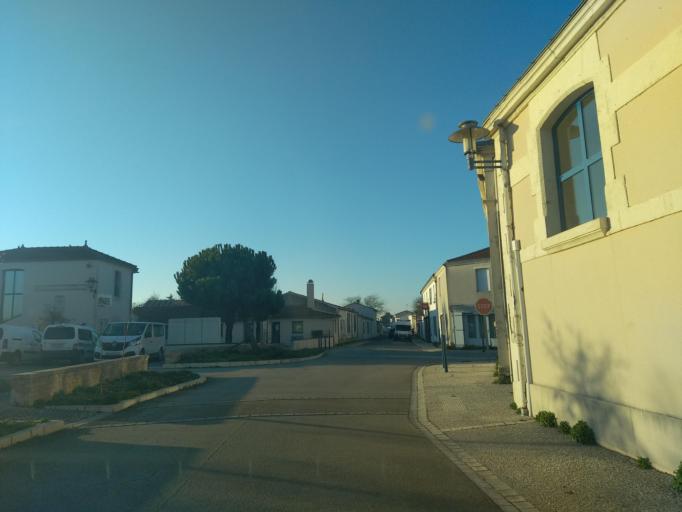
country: FR
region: Pays de la Loire
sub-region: Departement de la Vendee
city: Angles
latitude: 46.3976
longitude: -1.3037
